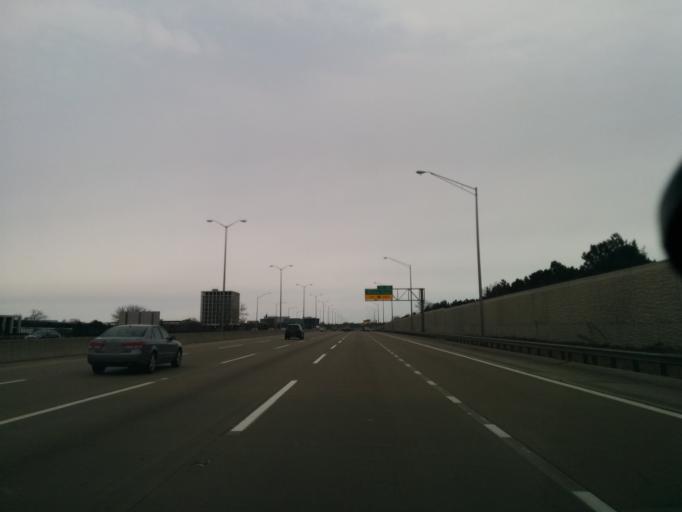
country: US
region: Illinois
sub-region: Cook County
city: Northbrook
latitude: 42.0953
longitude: -87.8680
